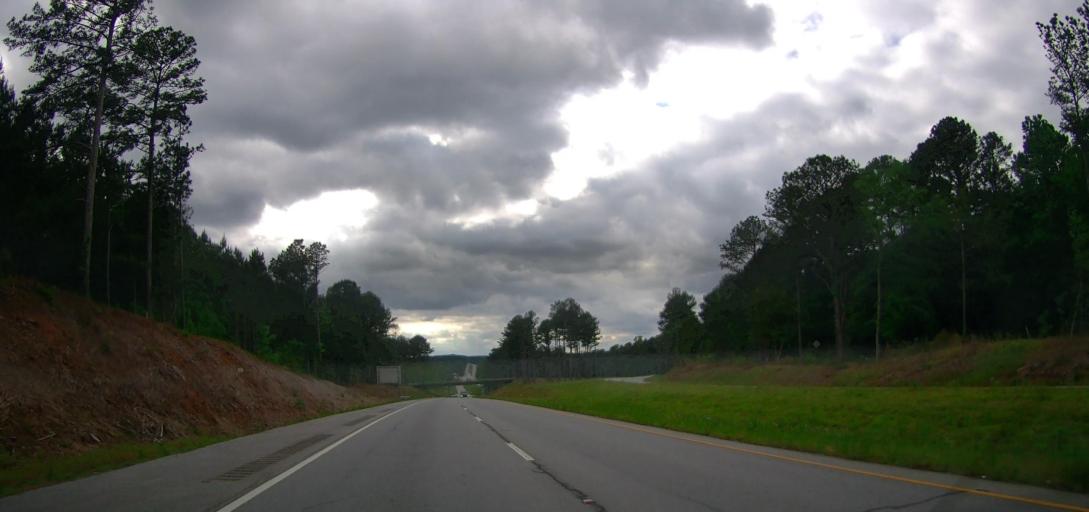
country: US
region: Georgia
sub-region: Walton County
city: Monroe
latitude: 33.8022
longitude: -83.7462
